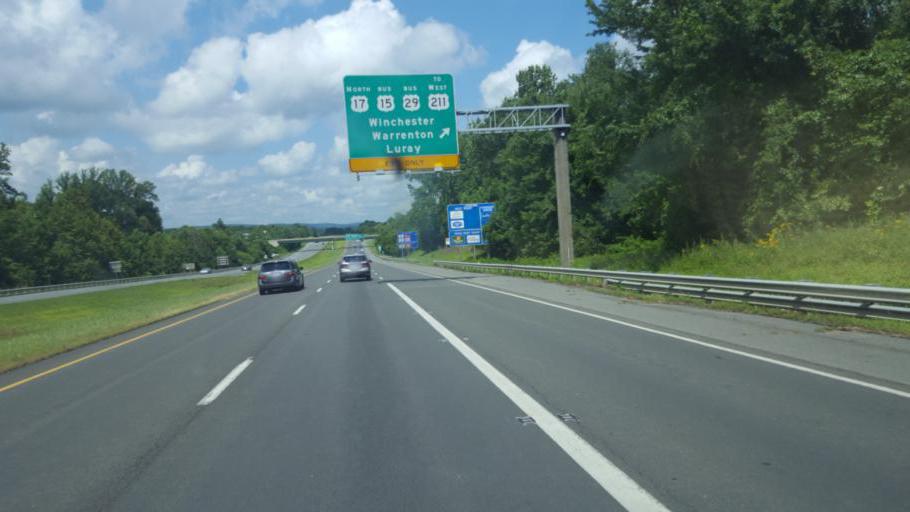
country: US
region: Virginia
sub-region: Fauquier County
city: Warrenton
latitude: 38.7134
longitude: -77.7808
